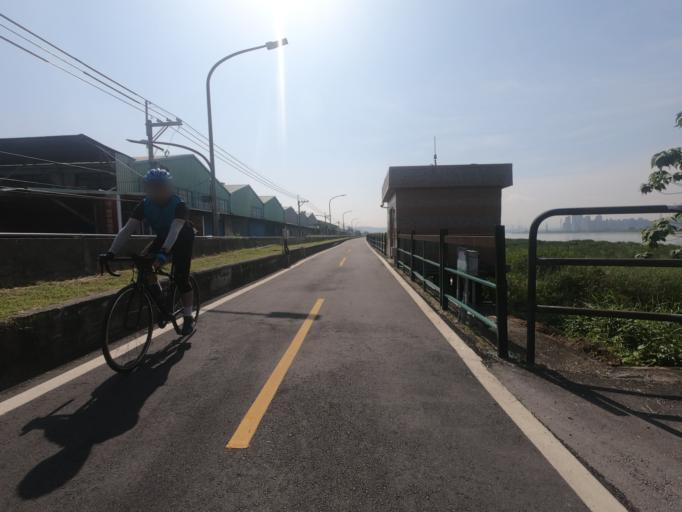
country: TW
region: Taipei
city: Taipei
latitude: 25.1051
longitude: 121.4770
